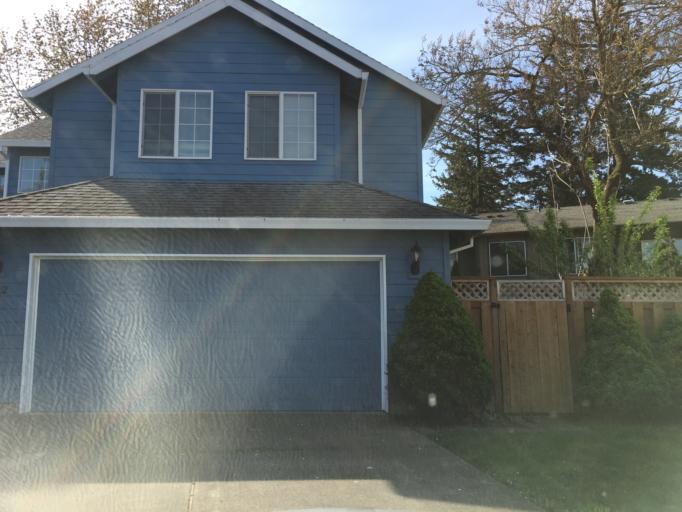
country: US
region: Oregon
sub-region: Multnomah County
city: Lents
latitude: 45.5349
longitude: -122.5455
